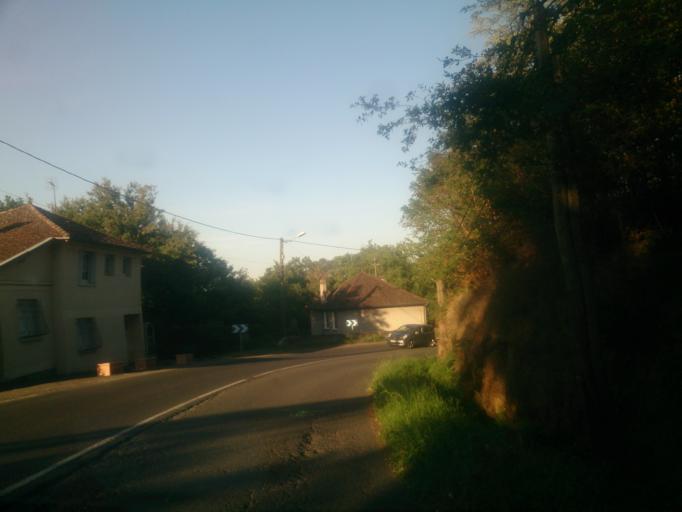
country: FR
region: Limousin
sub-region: Departement de la Correze
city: Brive-la-Gaillarde
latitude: 45.1457
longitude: 1.5280
